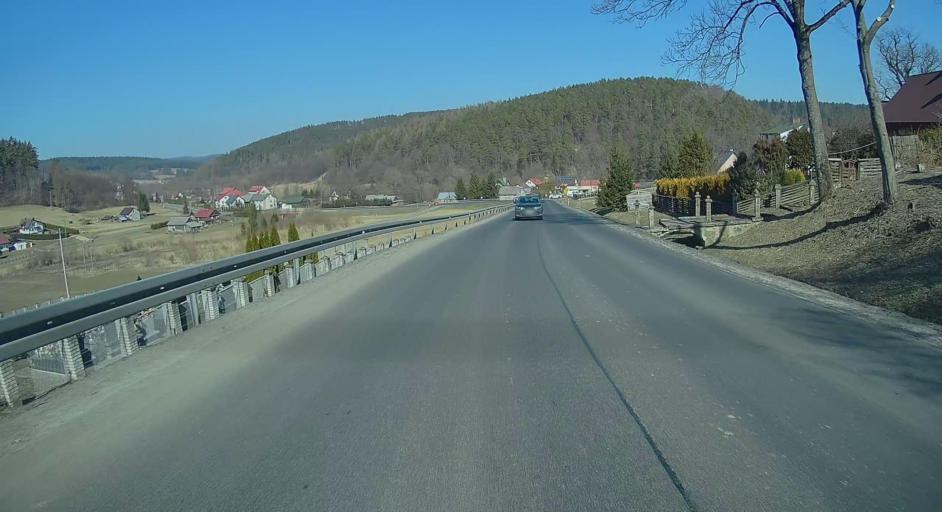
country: PL
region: Subcarpathian Voivodeship
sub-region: Powiat przemyski
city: Bircza
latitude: 49.6599
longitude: 22.4323
